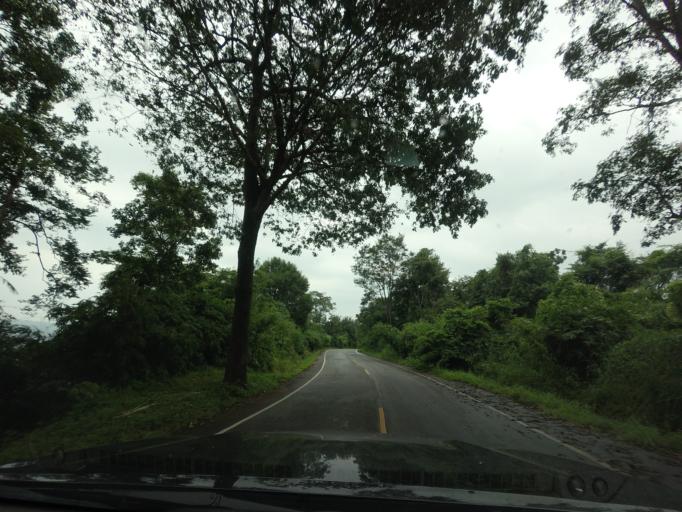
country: TH
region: Nong Khai
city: Sangkhom
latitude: 18.0387
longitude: 102.3268
